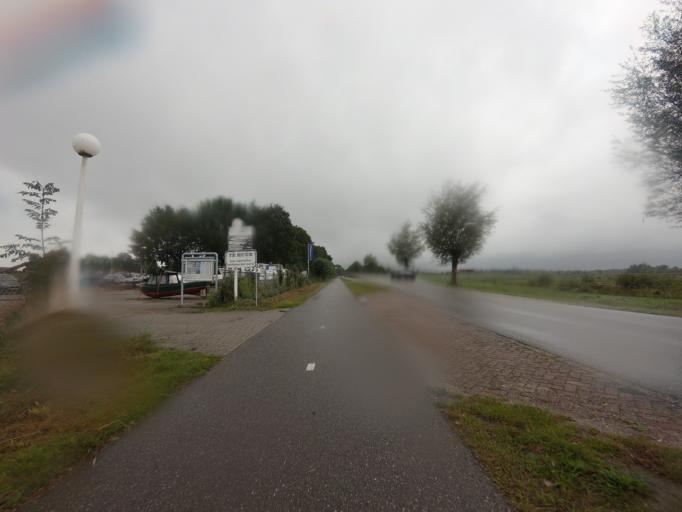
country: NL
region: Friesland
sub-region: Gemeente Tytsjerksteradiel
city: Garyp
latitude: 53.1351
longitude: 5.9463
